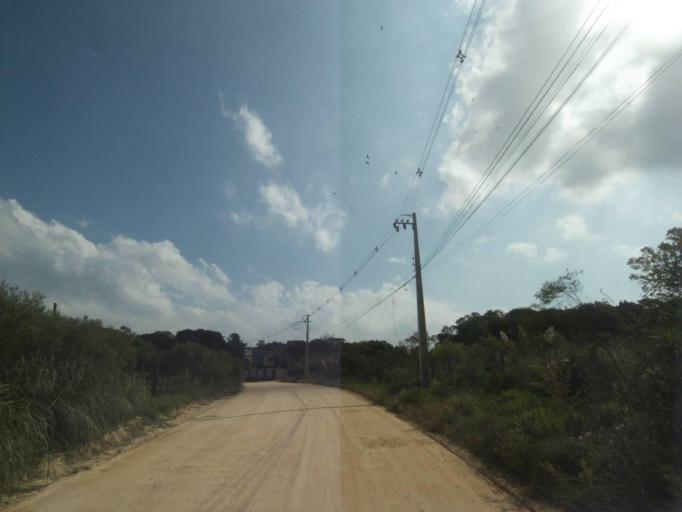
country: BR
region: Parana
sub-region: Araucaria
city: Araucaria
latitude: -25.5151
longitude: -49.3441
